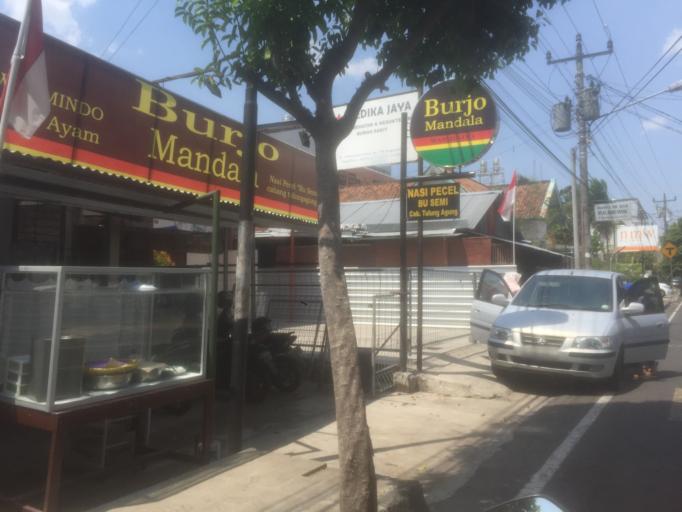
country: ID
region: Daerah Istimewa Yogyakarta
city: Yogyakarta
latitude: -7.7809
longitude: 110.3662
